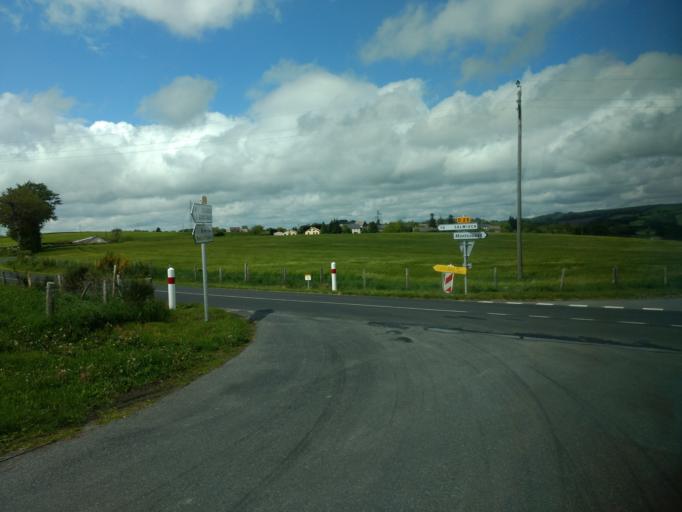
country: FR
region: Midi-Pyrenees
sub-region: Departement de l'Aveyron
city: Cassagnes-Begonhes
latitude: 44.1391
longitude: 2.6533
